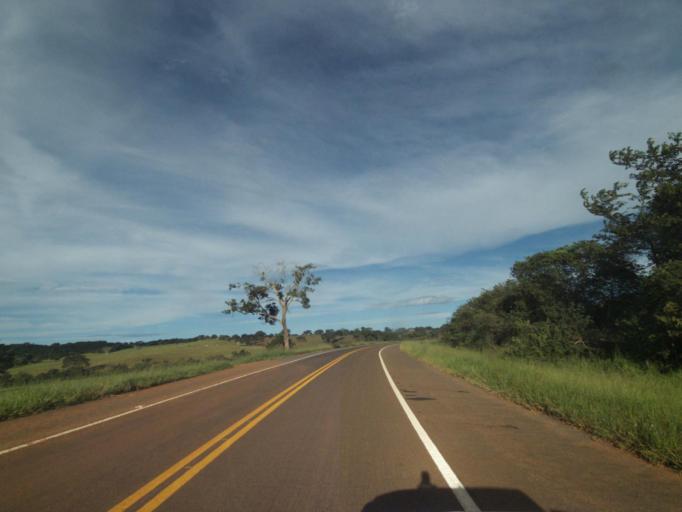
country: BR
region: Goias
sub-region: Jaragua
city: Jaragua
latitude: -15.8923
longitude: -49.5153
